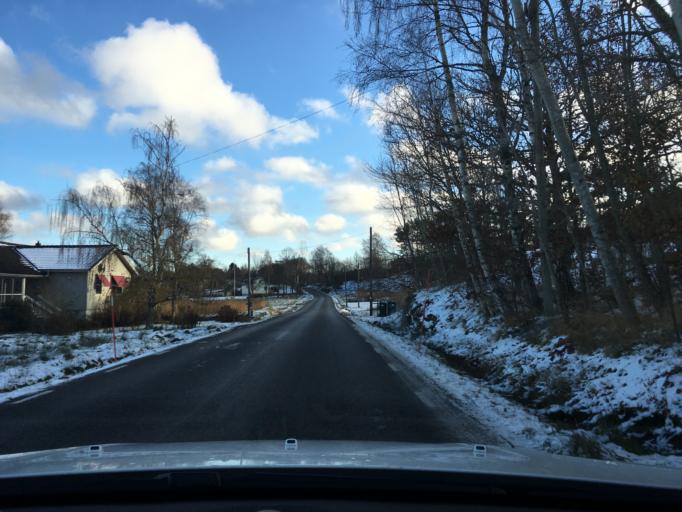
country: SE
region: Vaestra Goetaland
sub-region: Tjorns Kommun
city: Myggenas
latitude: 58.0547
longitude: 11.6976
